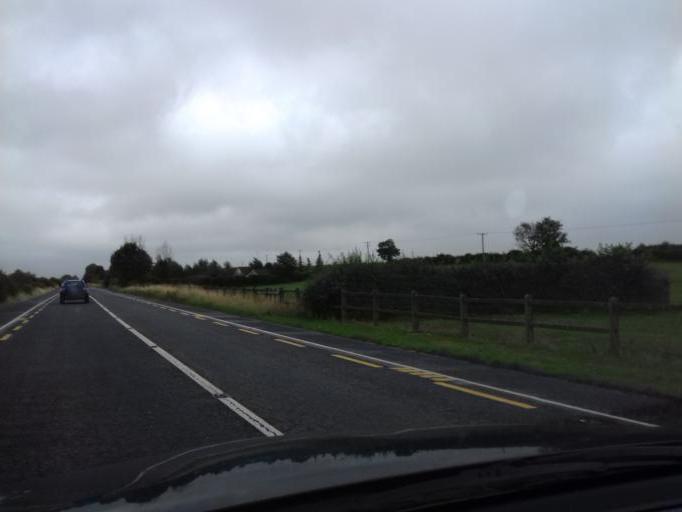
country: IE
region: Leinster
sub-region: County Carlow
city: Bagenalstown
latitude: 52.7490
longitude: -6.9660
